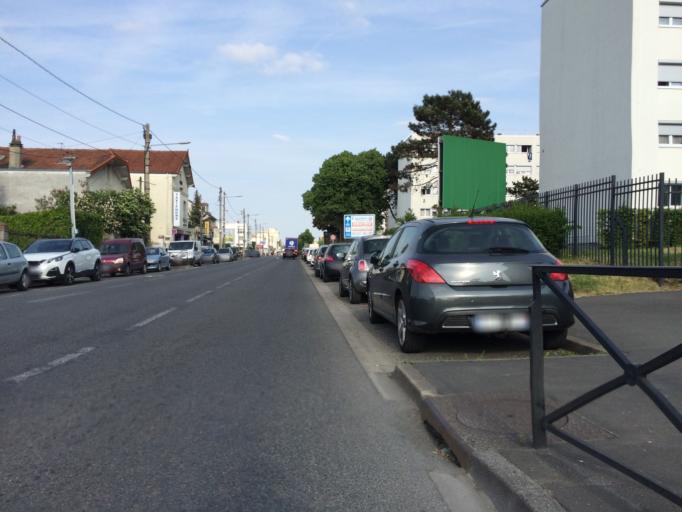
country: FR
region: Ile-de-France
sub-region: Departement de l'Essonne
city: Paray-Vieille-Poste
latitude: 48.7056
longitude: 2.3602
